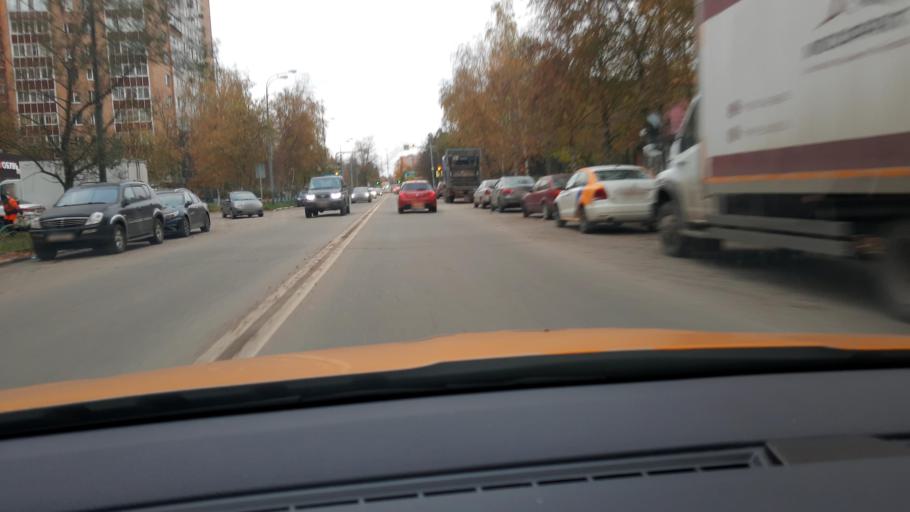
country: RU
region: Moskovskaya
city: Odintsovo
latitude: 55.6754
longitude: 37.2708
